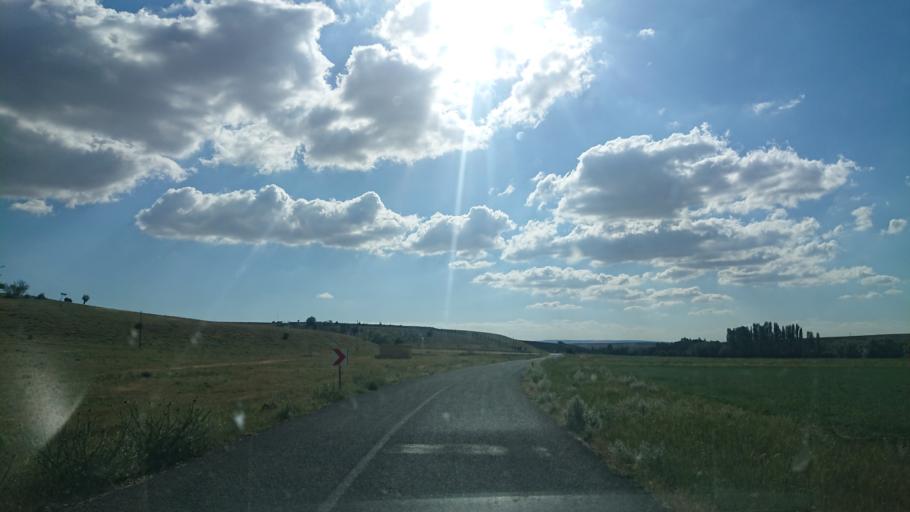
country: TR
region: Aksaray
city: Agacoren
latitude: 38.7560
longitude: 33.9176
